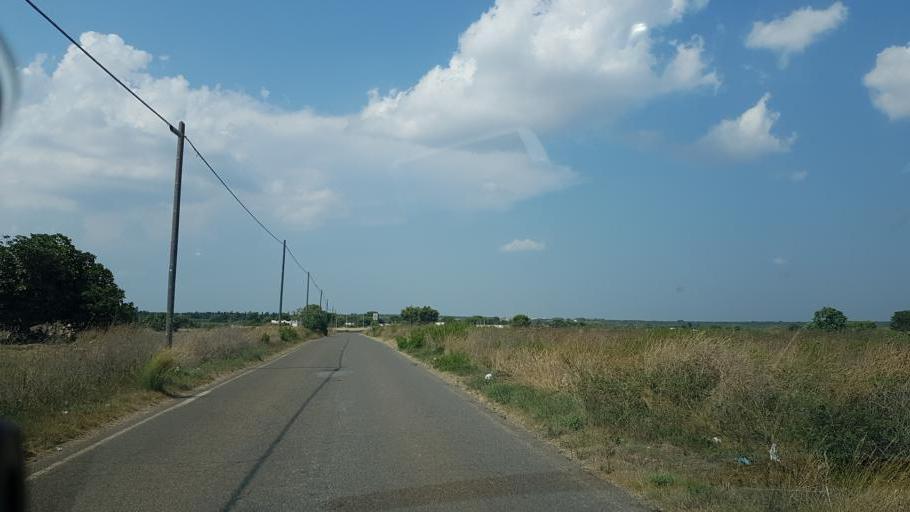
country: IT
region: Apulia
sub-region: Provincia di Taranto
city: Maruggio
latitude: 40.3088
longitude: 17.6330
